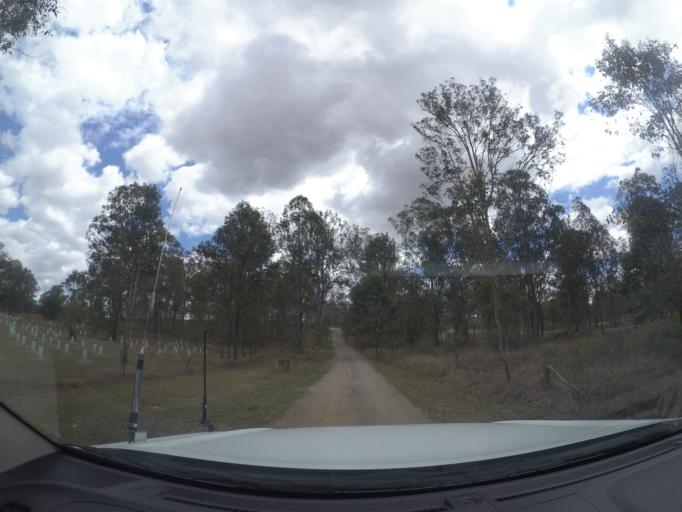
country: AU
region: Queensland
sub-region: Logan
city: Cedar Vale
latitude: -27.9258
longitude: 153.0789
